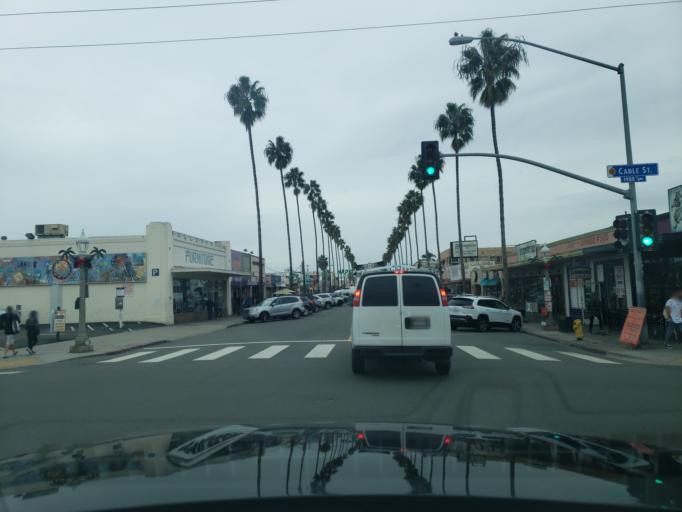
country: US
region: California
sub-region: San Diego County
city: Coronado
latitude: 32.7458
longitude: -117.2493
